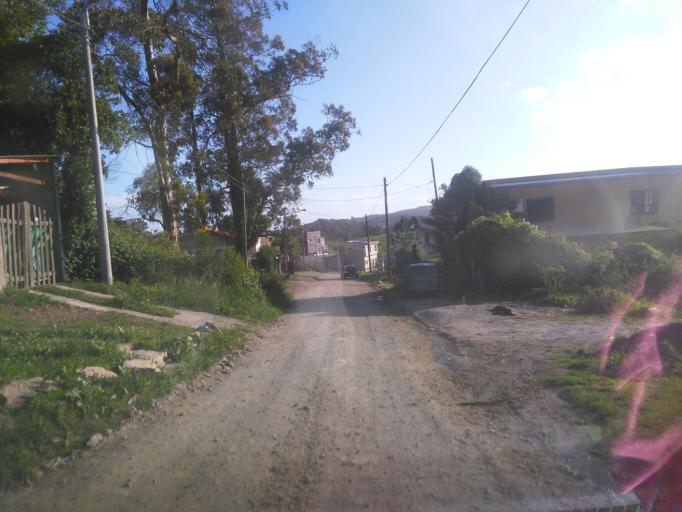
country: AR
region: Buenos Aires
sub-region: Partido de Tandil
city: Tandil
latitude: -37.3419
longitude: -59.1403
